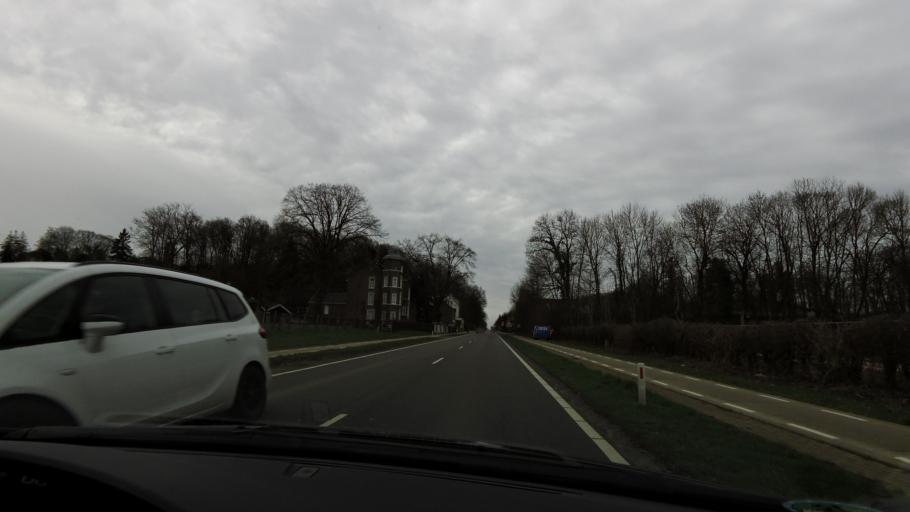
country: NL
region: Limburg
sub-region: Gemeente Maastricht
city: Heer
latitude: 50.8382
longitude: 5.7513
